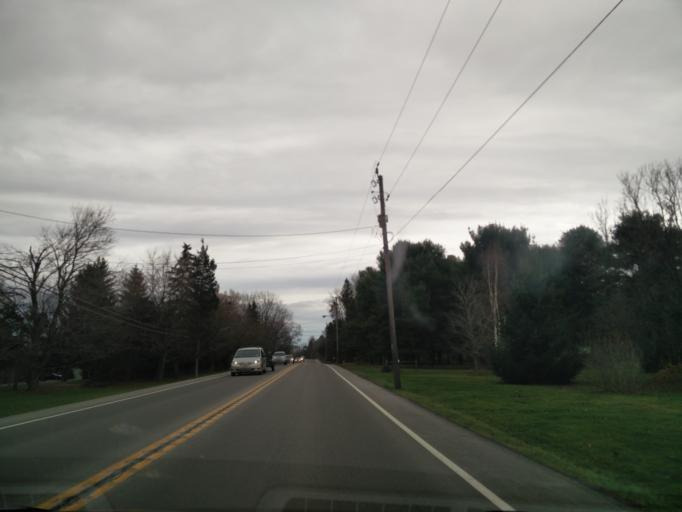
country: US
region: New York
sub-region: Tompkins County
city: Northwest Ithaca
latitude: 42.4782
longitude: -76.5588
